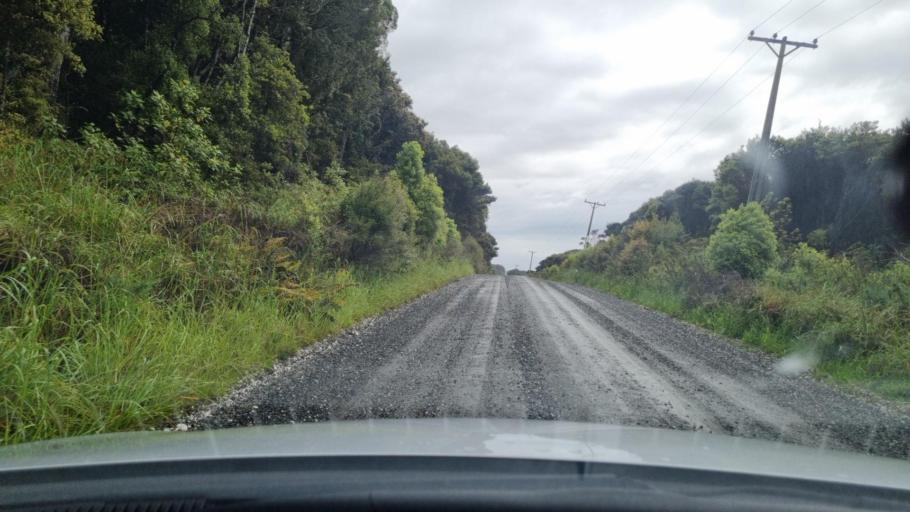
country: NZ
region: Southland
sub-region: Invercargill City
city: Bluff
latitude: -46.5416
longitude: 168.2635
